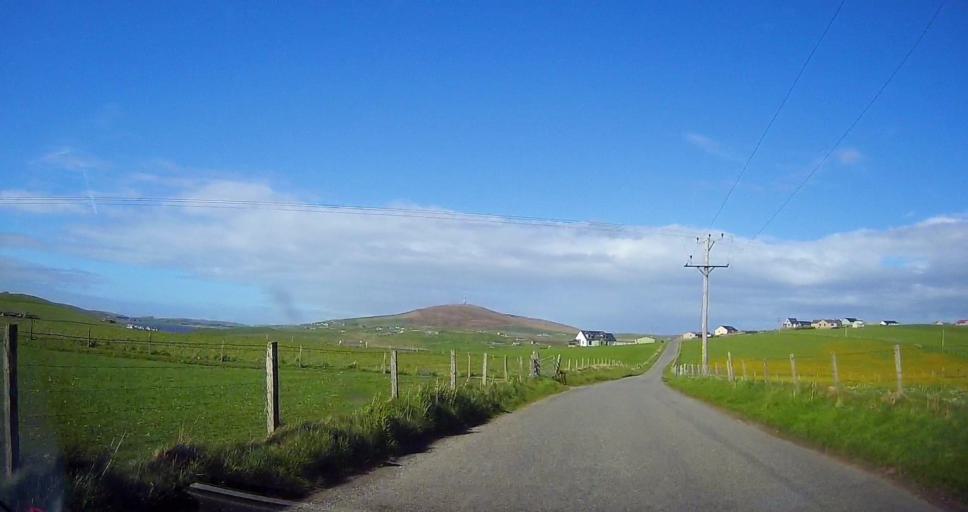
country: GB
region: Scotland
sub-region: Shetland Islands
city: Sandwick
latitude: 59.9136
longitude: -1.3236
